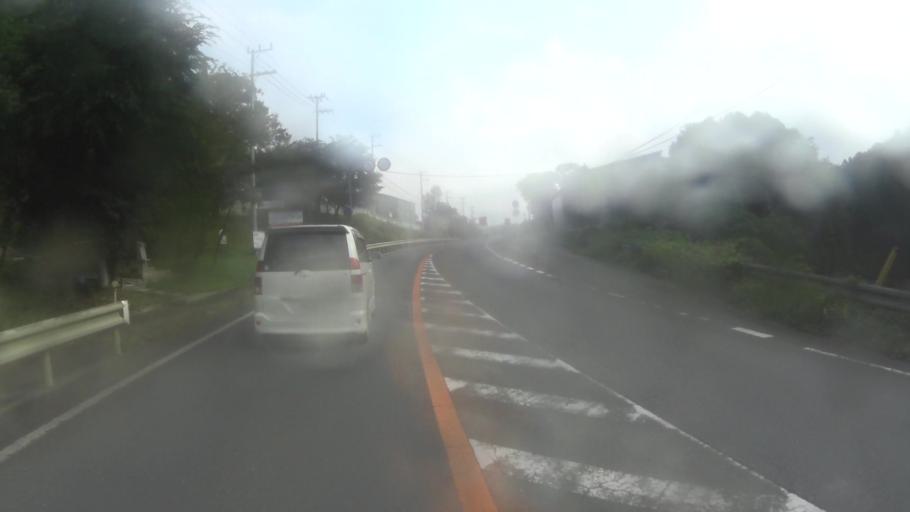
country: JP
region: Kyoto
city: Ayabe
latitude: 35.1959
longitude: 135.4181
